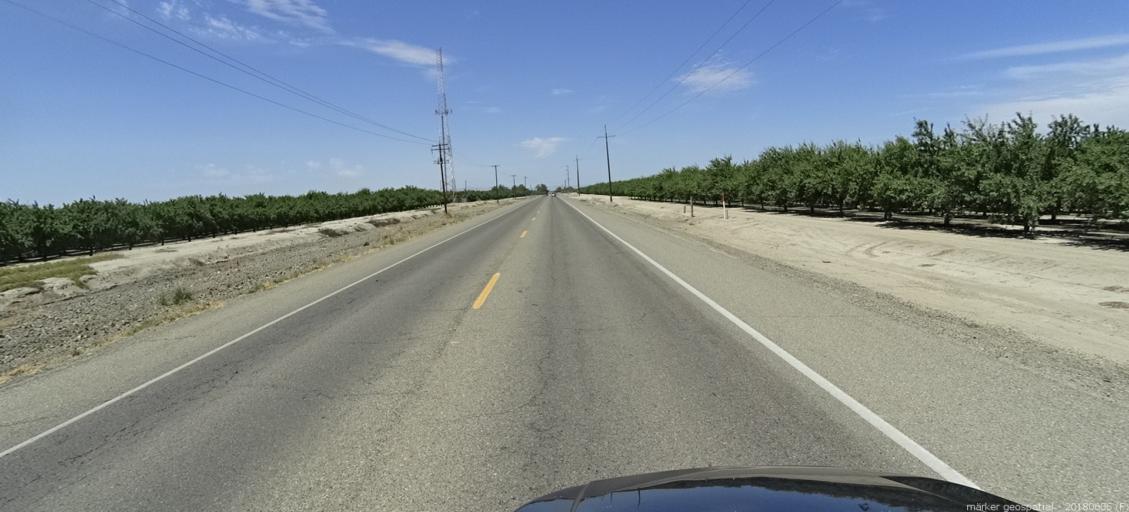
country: US
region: California
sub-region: Fresno County
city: Firebaugh
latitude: 36.8586
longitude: -120.3934
